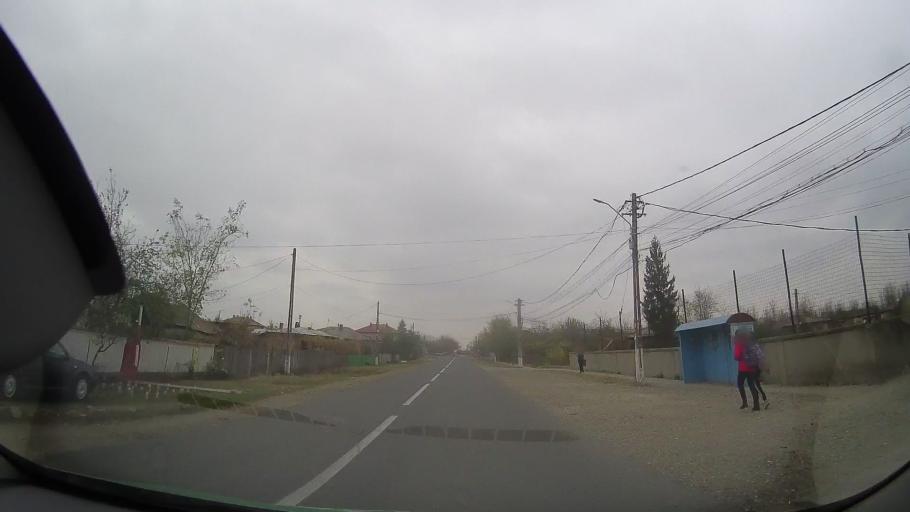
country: RO
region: Ialomita
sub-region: Comuna Garbovi
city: Garbovi
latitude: 44.7860
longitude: 26.7641
